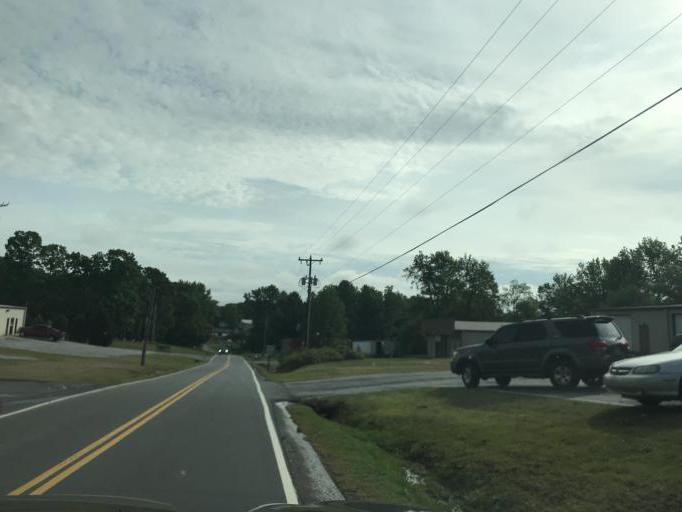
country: US
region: South Carolina
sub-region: Spartanburg County
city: Roebuck
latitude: 34.9111
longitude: -81.9549
